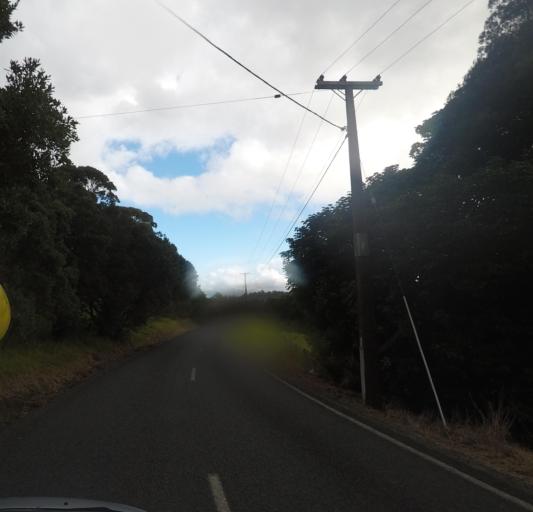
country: NZ
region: Auckland
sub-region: Auckland
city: Warkworth
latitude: -36.3774
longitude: 174.7600
